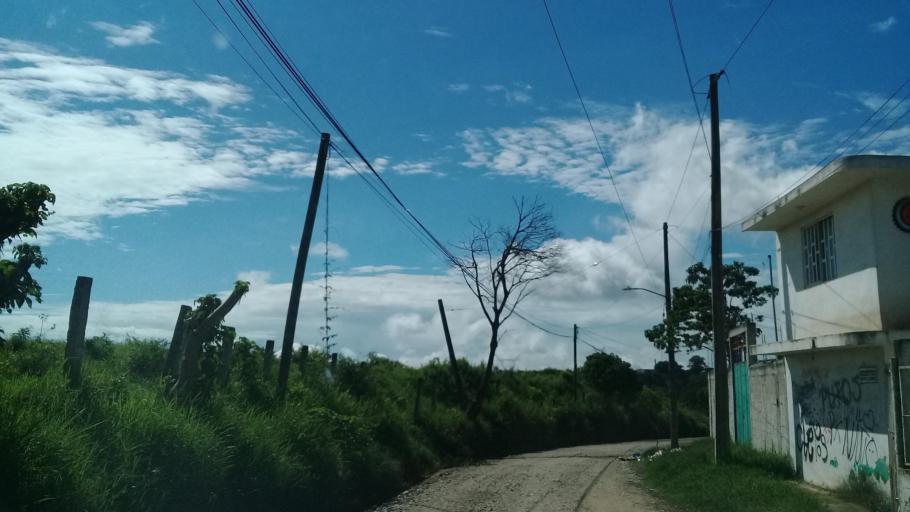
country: MX
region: Veracruz
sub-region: Jilotepec
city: El Pueblito (Garbanzal)
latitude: 19.5739
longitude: -96.8993
